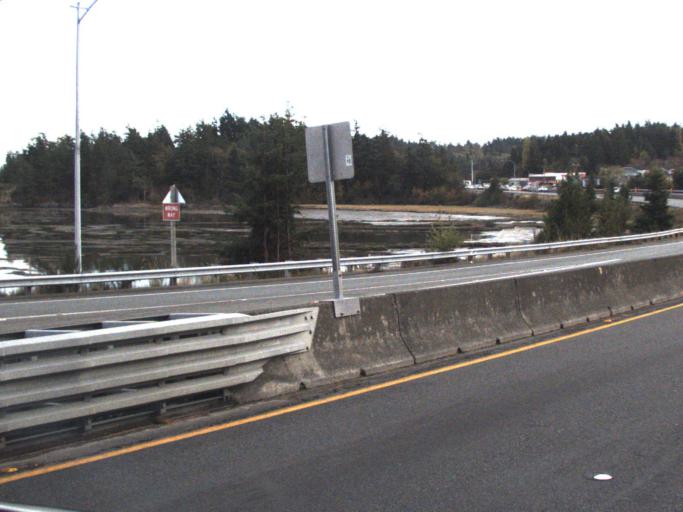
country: US
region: Washington
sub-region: Jefferson County
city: Port Hadlock-Irondale
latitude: 47.9896
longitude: -122.8817
